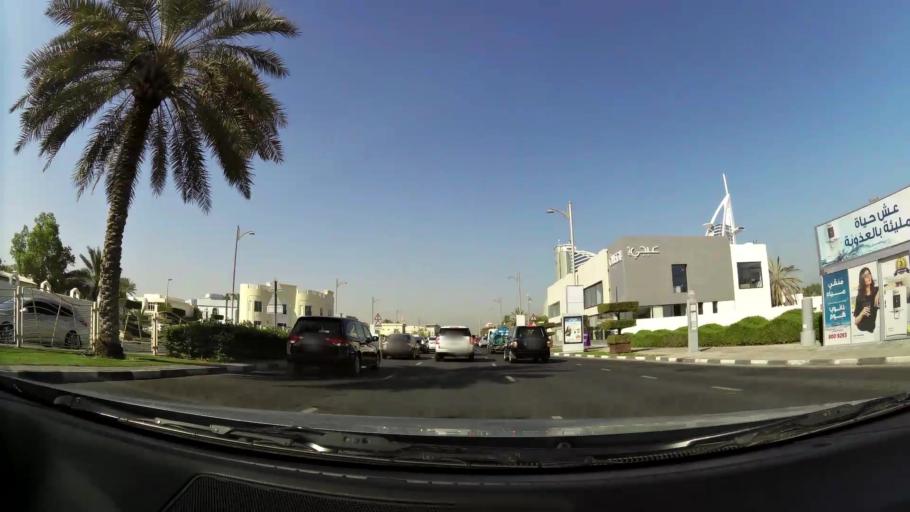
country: AE
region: Dubai
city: Dubai
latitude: 25.1441
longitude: 55.1941
